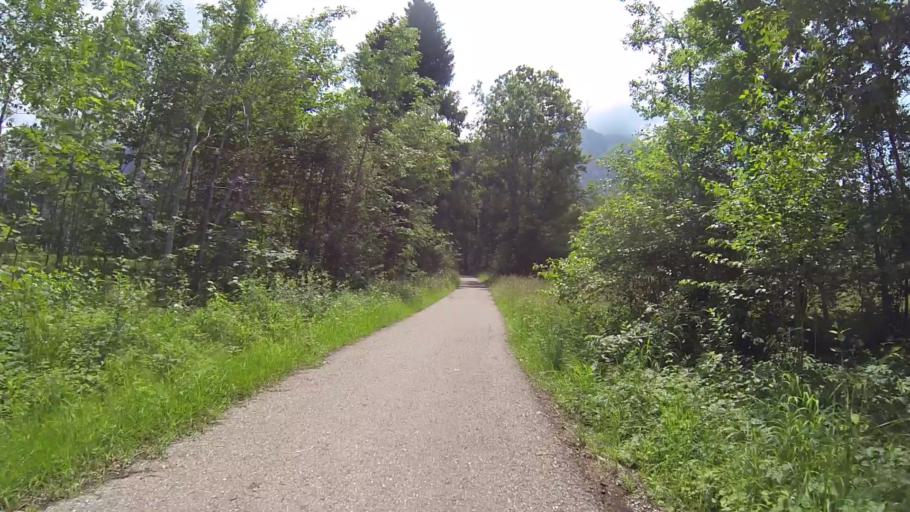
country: DE
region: Bavaria
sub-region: Swabia
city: Schwangau
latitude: 47.5615
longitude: 10.7290
